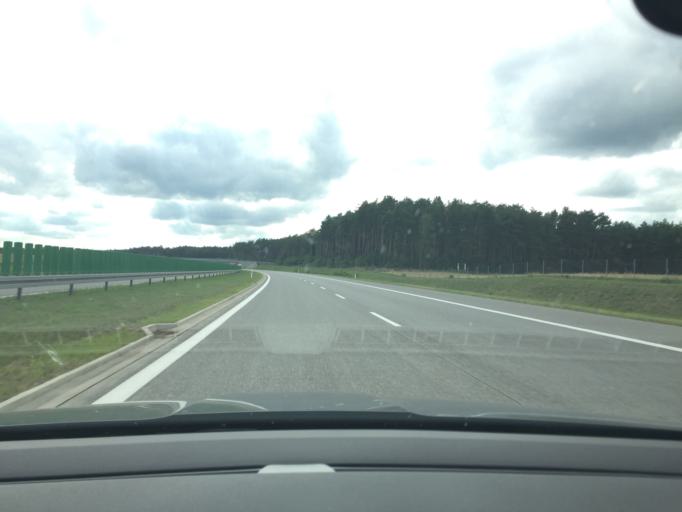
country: PL
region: Lubusz
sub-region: Powiat sulecinski
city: Torzym
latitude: 52.3378
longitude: 14.9599
